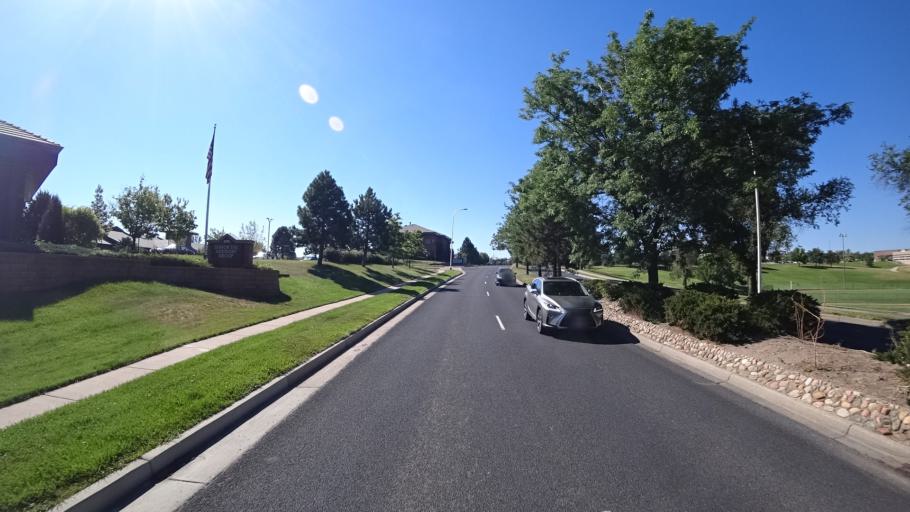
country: US
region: Colorado
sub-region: El Paso County
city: Cimarron Hills
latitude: 38.9292
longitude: -104.7526
